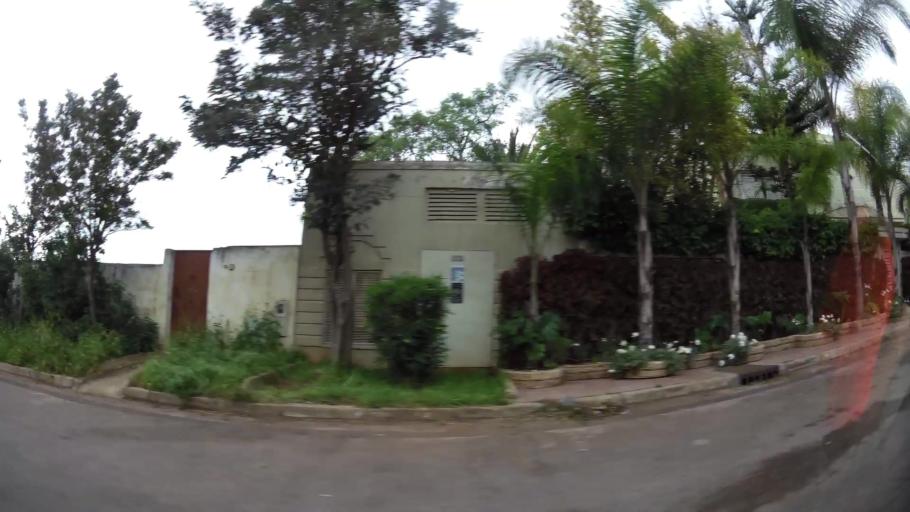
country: MA
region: Grand Casablanca
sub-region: Casablanca
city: Casablanca
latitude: 33.5260
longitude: -7.6341
